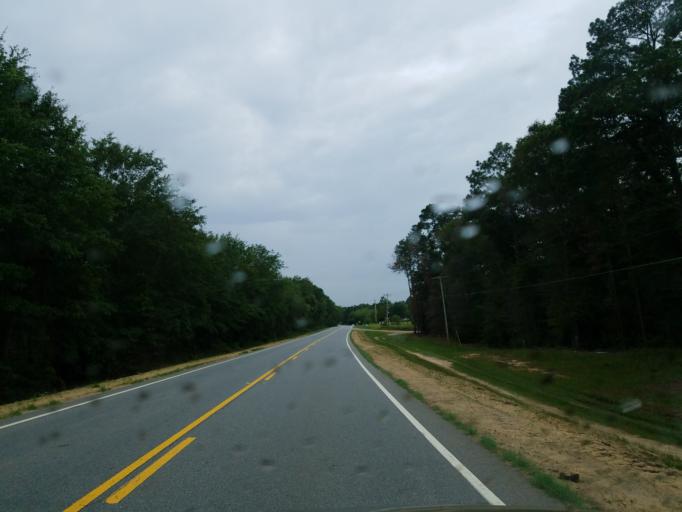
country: US
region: Georgia
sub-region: Crisp County
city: Cordele
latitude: 32.0218
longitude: -83.7246
